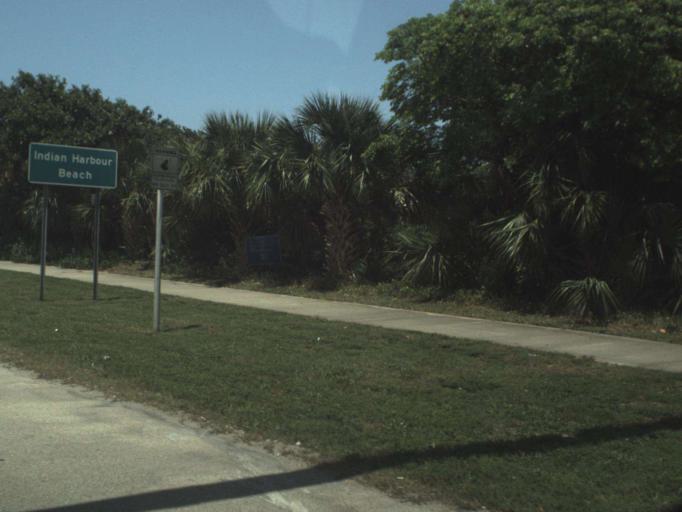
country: US
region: Florida
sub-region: Brevard County
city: Indian Harbour Beach
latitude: 28.1389
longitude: -80.5810
